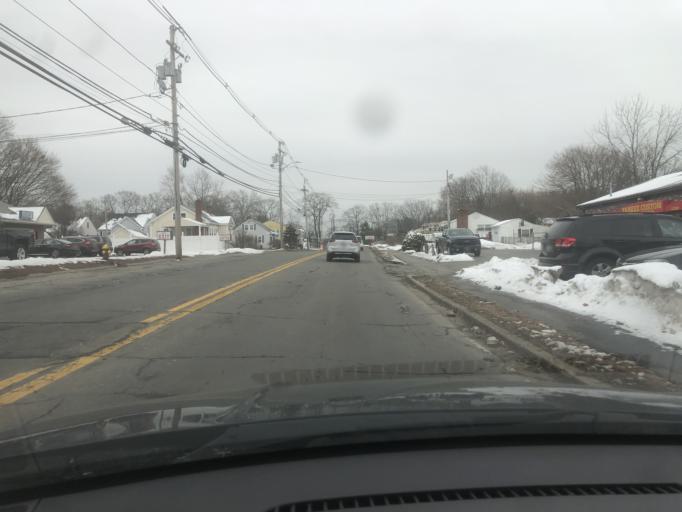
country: US
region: Massachusetts
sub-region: Middlesex County
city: Tewksbury
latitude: 42.6058
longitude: -71.2255
